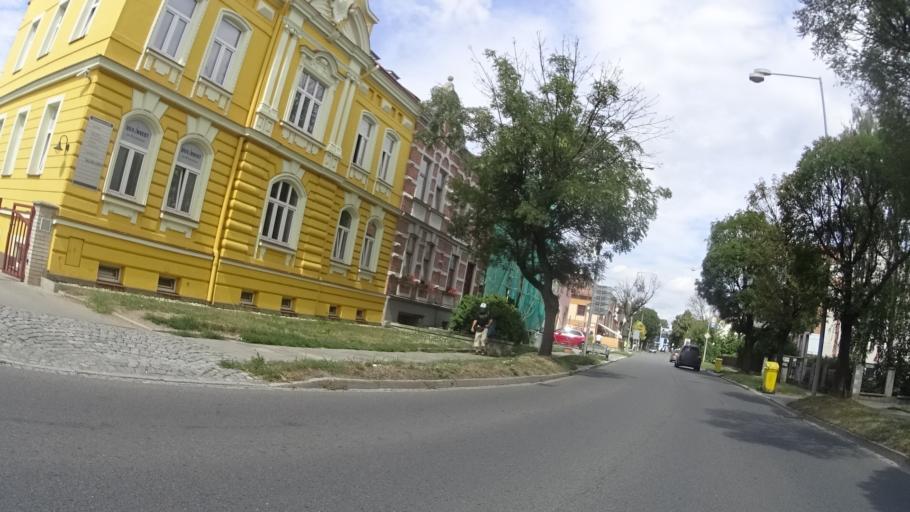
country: CZ
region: Olomoucky
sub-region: Okres Olomouc
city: Olomouc
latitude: 49.5822
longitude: 17.2495
